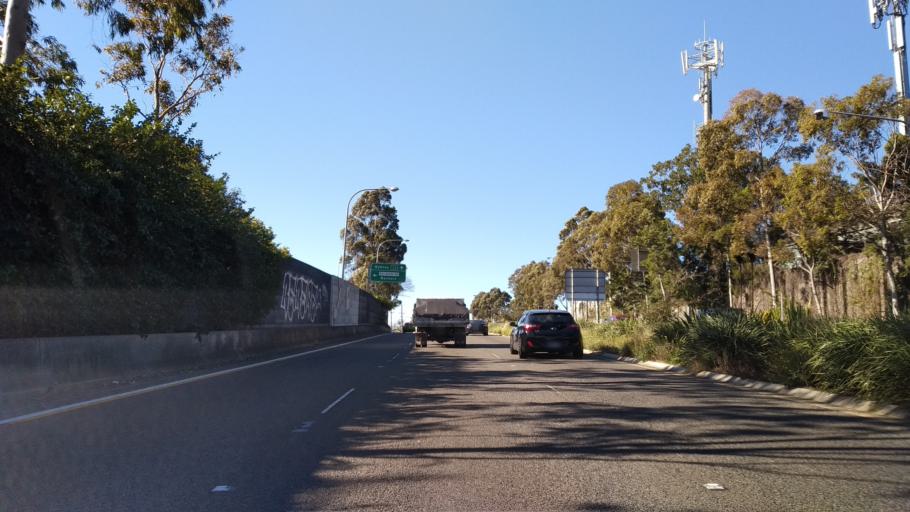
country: AU
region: New South Wales
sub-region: Leichhardt
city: Leichhardt
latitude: -33.8751
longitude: 151.1584
